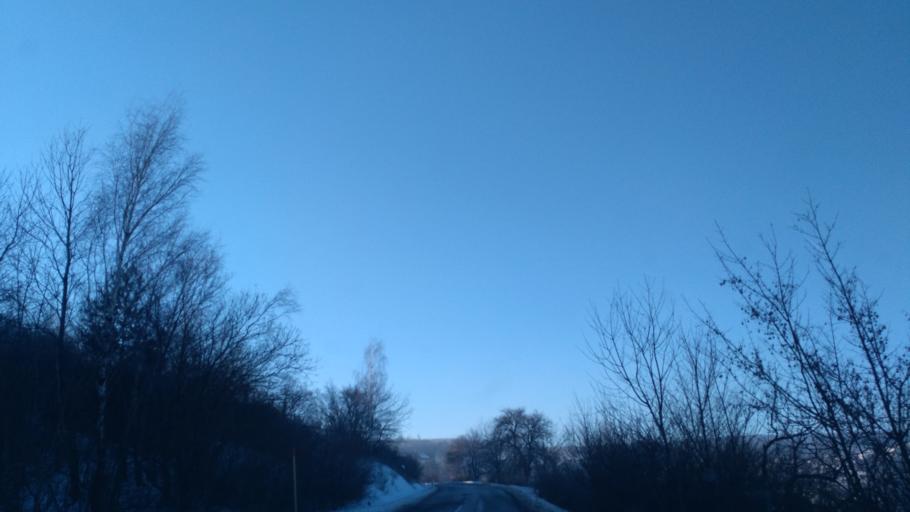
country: SK
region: Kosicky
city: Kosice
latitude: 48.7718
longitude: 21.2187
